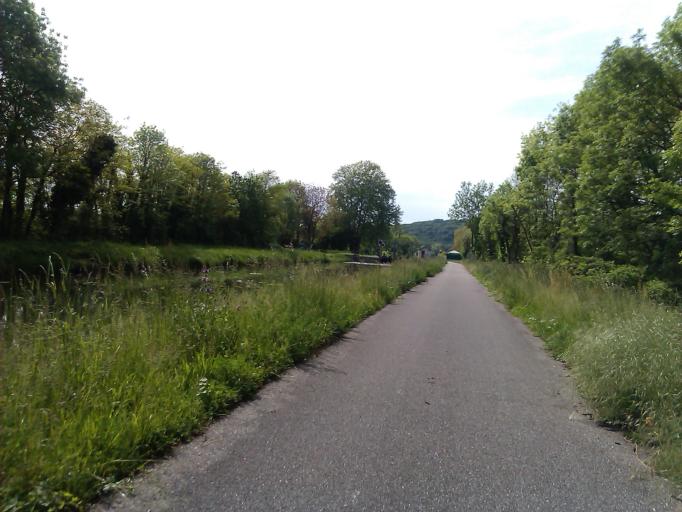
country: FR
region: Franche-Comte
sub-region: Departement du Doubs
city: Quingey
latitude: 47.1391
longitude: 5.8611
